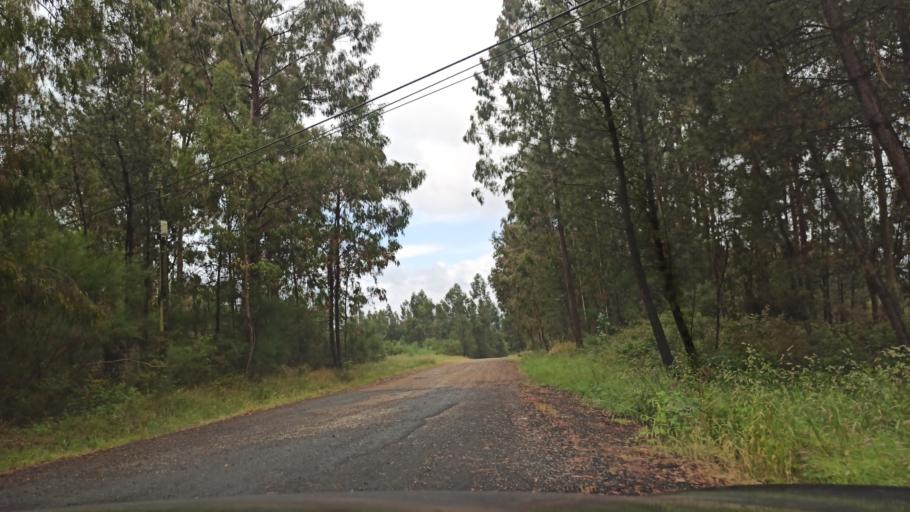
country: ES
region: Galicia
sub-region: Provincia da Coruna
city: Santiso
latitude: 42.7686
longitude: -8.0246
